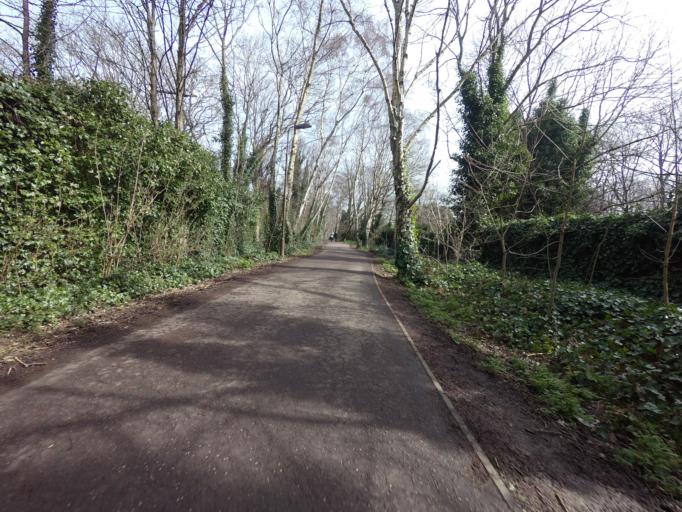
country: GB
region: Scotland
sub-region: Edinburgh
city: Edinburgh
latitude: 55.9674
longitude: -3.1978
